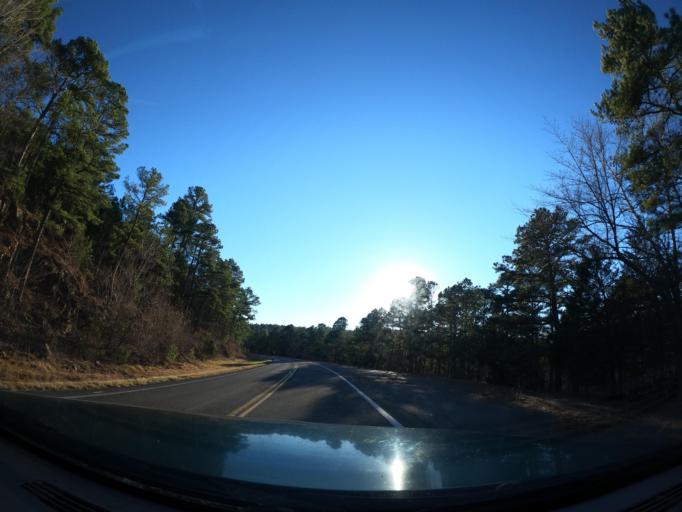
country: US
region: Oklahoma
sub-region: Latimer County
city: Wilburton
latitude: 34.9688
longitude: -95.3568
